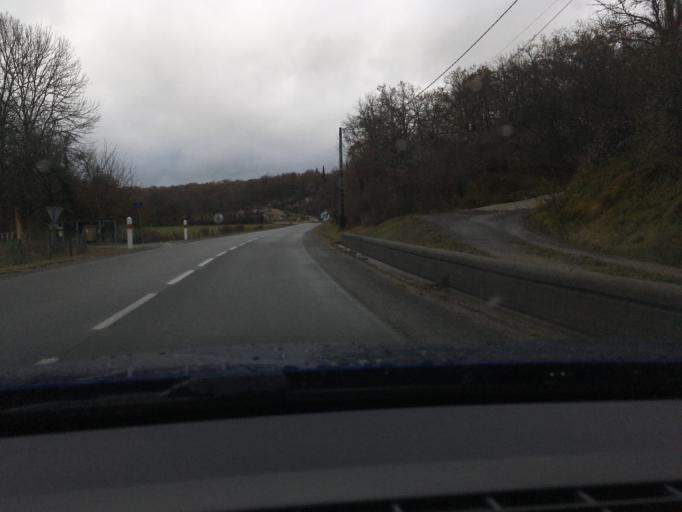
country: FR
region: Midi-Pyrenees
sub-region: Departement de l'Aveyron
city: Villefranche-de-Rouergue
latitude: 44.3680
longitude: 2.0156
